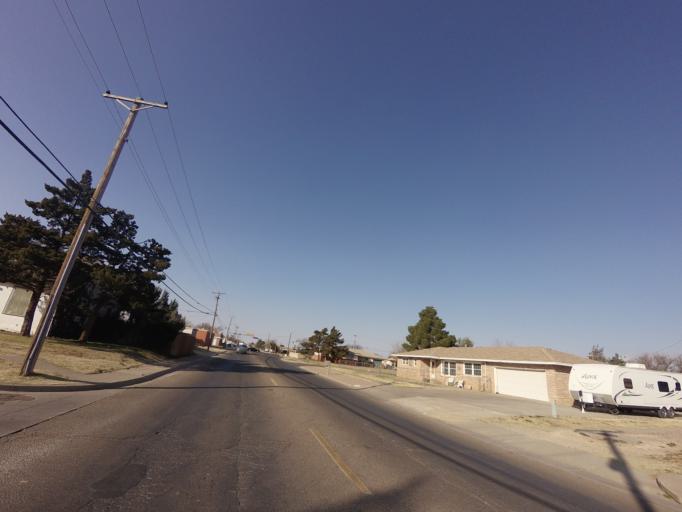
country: US
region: New Mexico
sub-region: Curry County
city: Clovis
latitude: 34.4120
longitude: -103.2129
